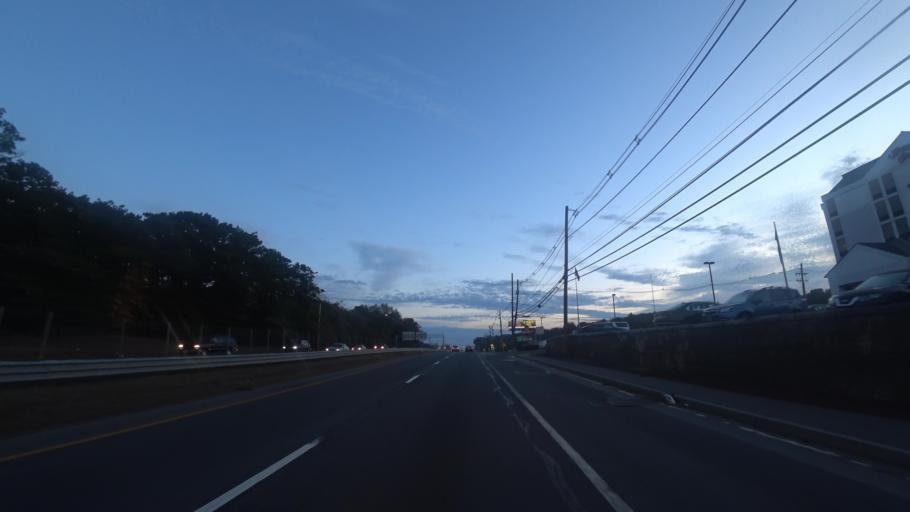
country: US
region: Massachusetts
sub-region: Essex County
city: South Peabody
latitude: 42.5263
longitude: -70.9948
